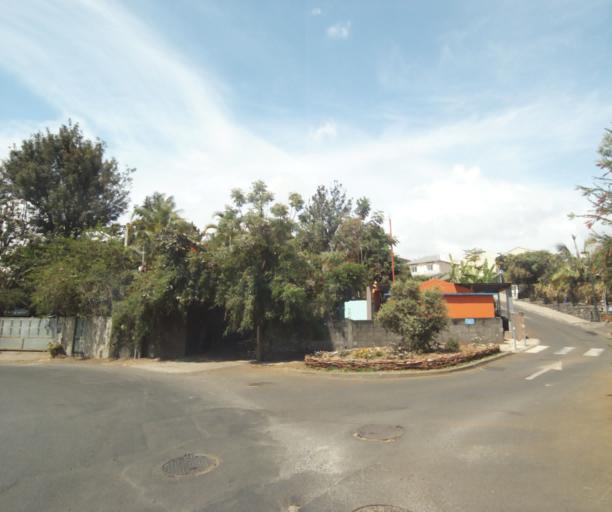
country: RE
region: Reunion
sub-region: Reunion
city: Trois-Bassins
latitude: -21.0772
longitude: 55.2692
